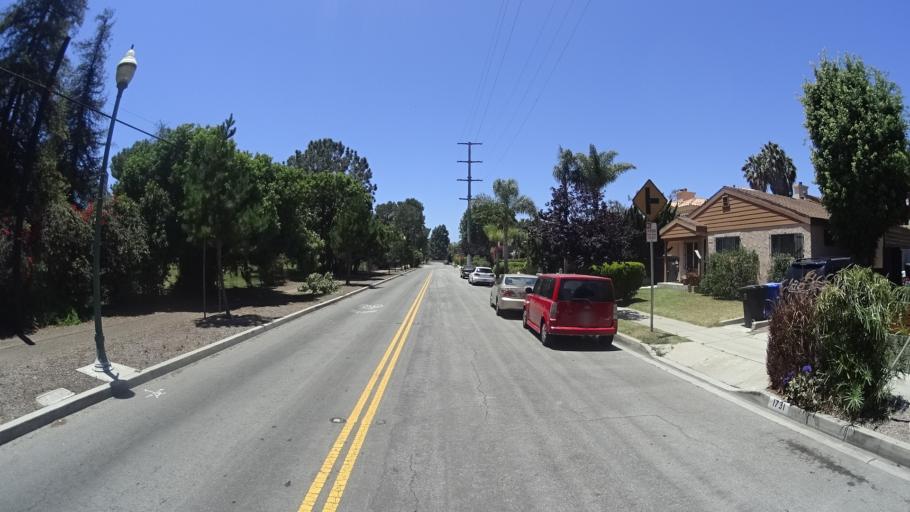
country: US
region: California
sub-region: Los Angeles County
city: Marina del Rey
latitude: 34.0071
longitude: -118.4617
